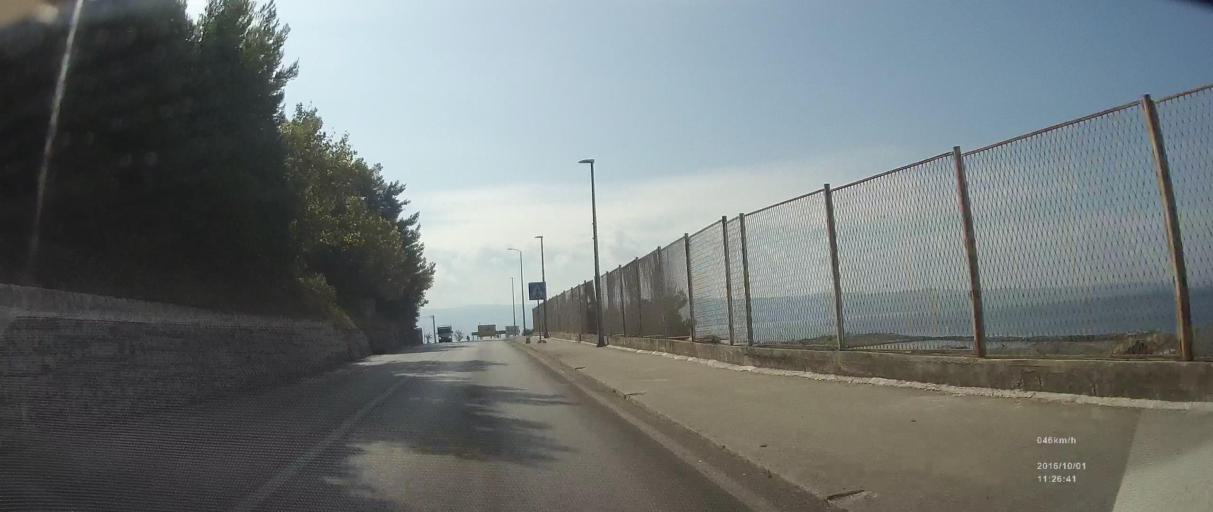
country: HR
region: Splitsko-Dalmatinska
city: Duce
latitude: 43.4412
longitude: 16.6434
